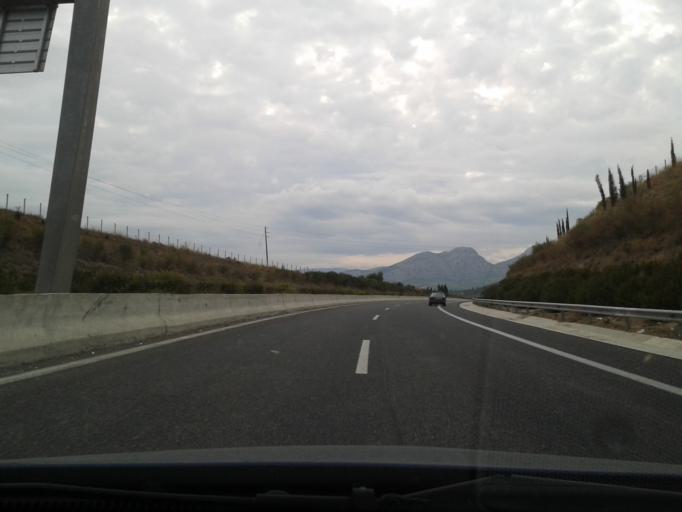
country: GR
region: Peloponnese
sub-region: Nomos Korinthias
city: Arkhaia Korinthos
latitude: 37.9060
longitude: 22.9059
